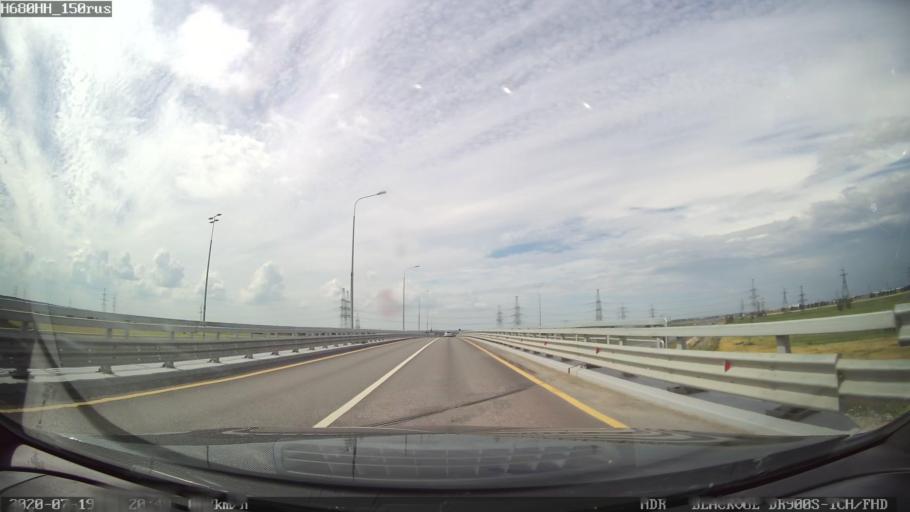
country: RU
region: Leningrad
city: Fedorovskoye
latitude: 59.7072
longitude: 30.5445
